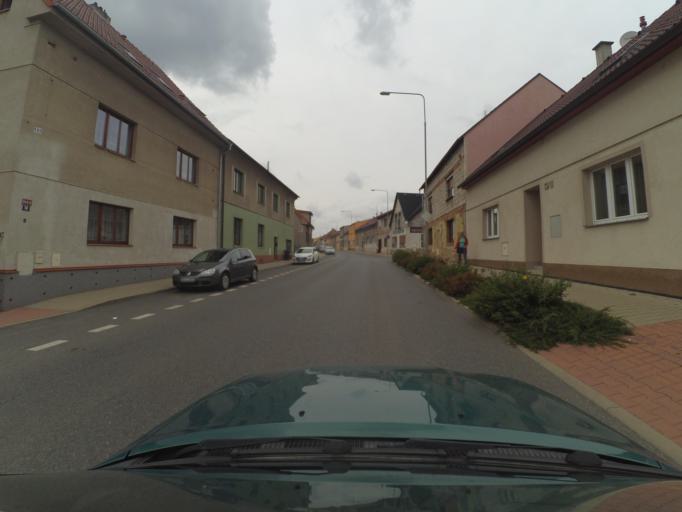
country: CZ
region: Central Bohemia
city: Rakovnik
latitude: 50.1043
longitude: 13.7356
